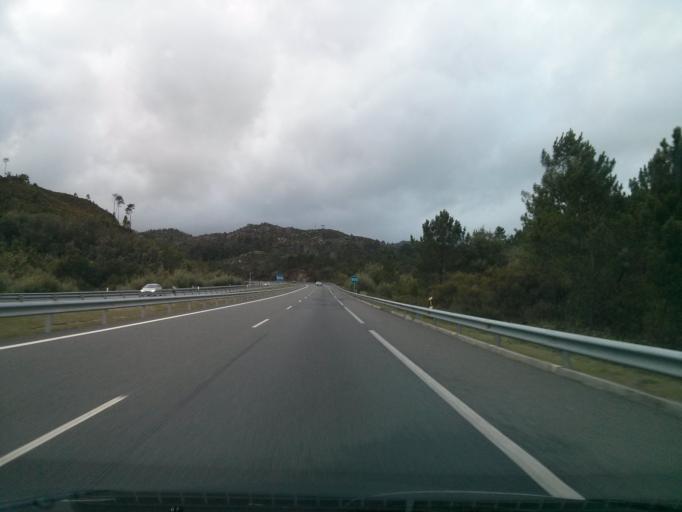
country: ES
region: Galicia
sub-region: Provincia de Ourense
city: Carballeda de Avia
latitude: 42.3098
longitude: -8.1660
